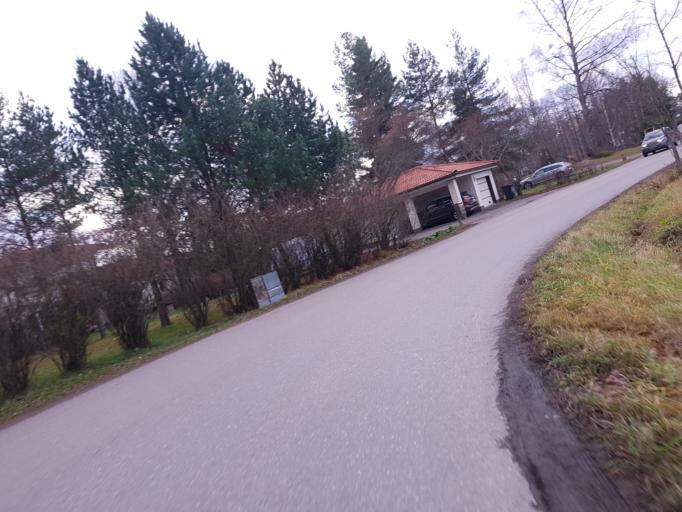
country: FI
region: Uusimaa
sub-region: Helsinki
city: Helsinki
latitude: 60.2802
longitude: 24.9220
